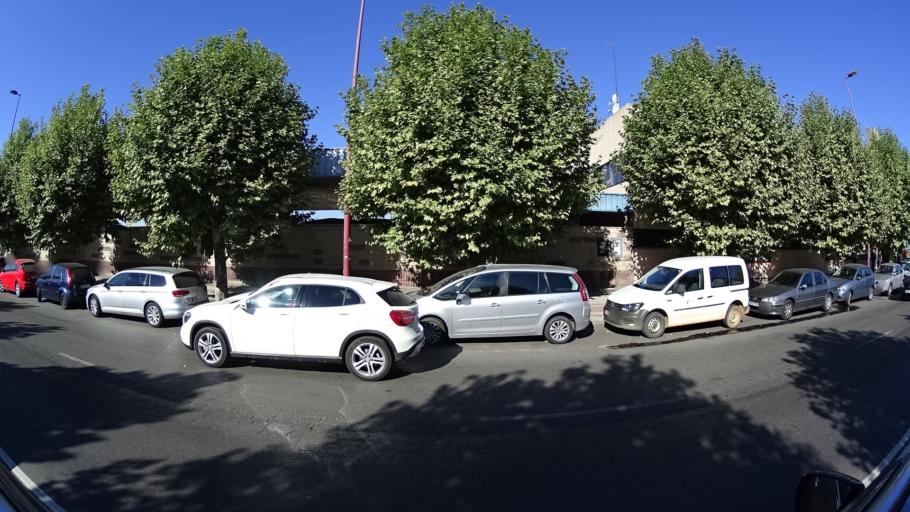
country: ES
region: Castille and Leon
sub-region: Provincia de Leon
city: Leon
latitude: 42.5932
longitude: -5.5786
